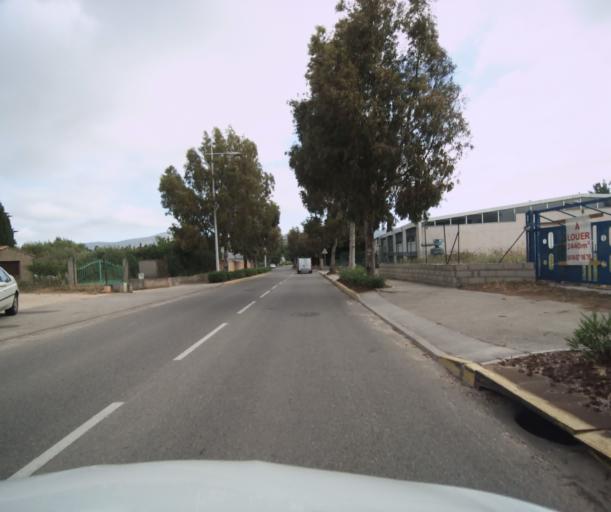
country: FR
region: Provence-Alpes-Cote d'Azur
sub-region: Departement du Var
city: Six-Fours-les-Plages
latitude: 43.1140
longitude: 5.8426
